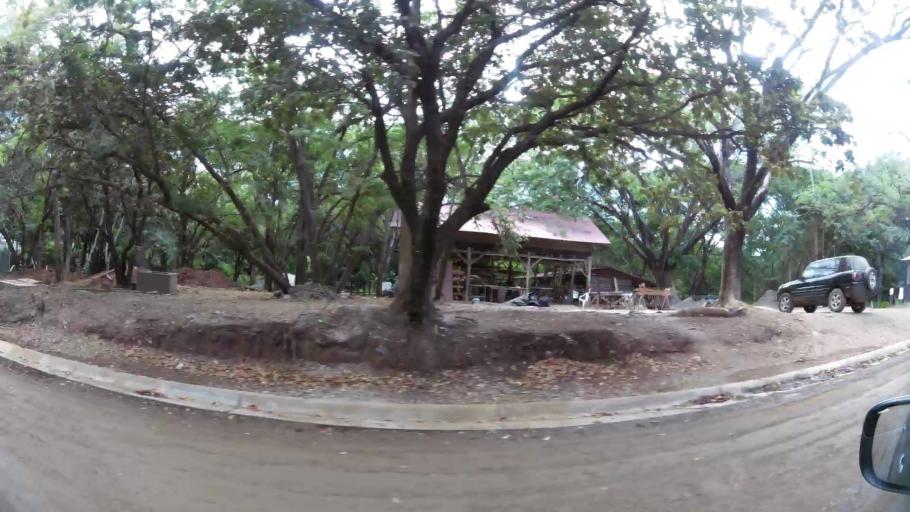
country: CR
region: Guanacaste
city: Santa Cruz
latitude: 10.2934
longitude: -85.8478
